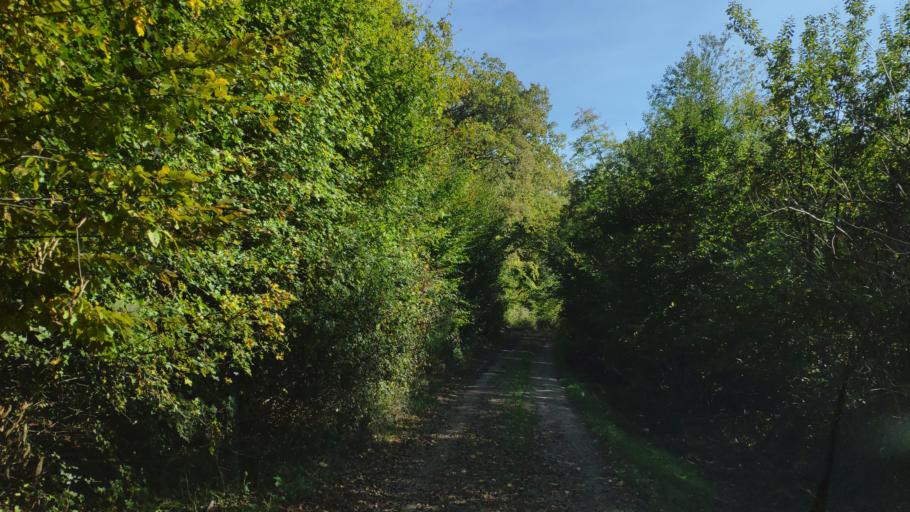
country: SK
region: Presovsky
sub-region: Okres Presov
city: Presov
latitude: 48.8845
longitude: 21.2262
